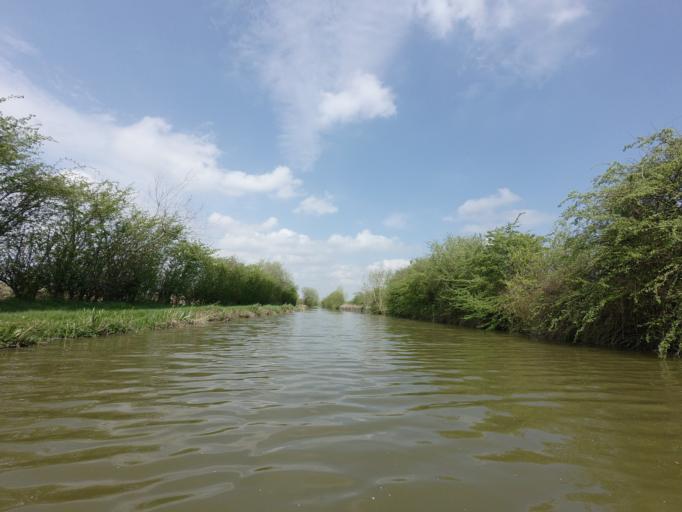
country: GB
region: England
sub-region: Central Bedfordshire
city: Leighton Buzzard
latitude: 51.8833
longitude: -0.6559
